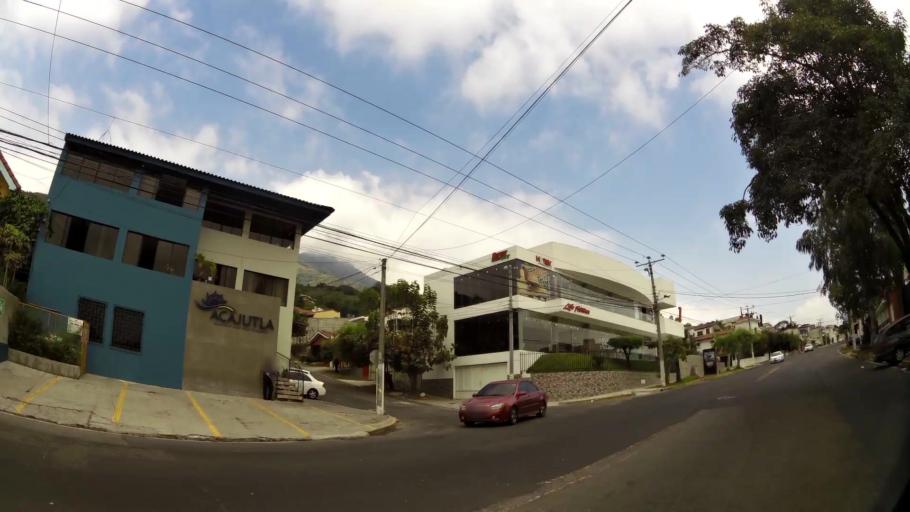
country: SV
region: San Salvador
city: Mejicanos
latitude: 13.7166
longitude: -89.2461
